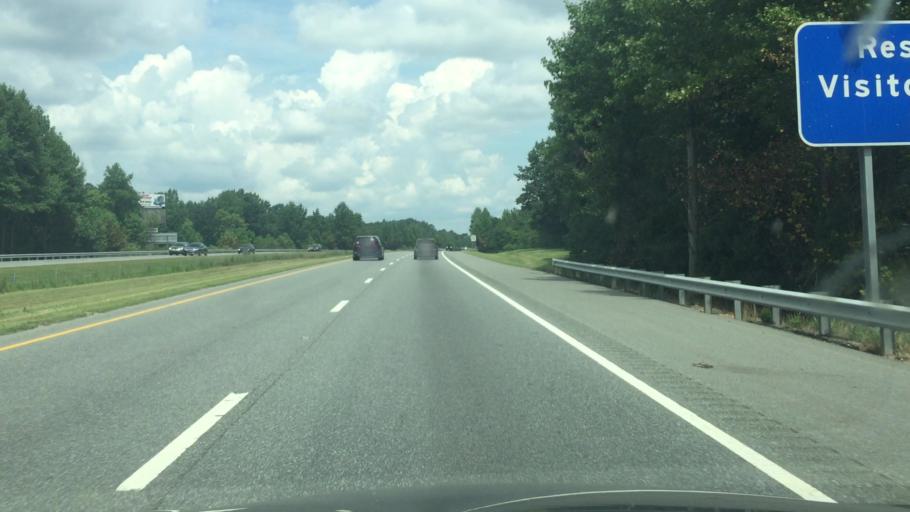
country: US
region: North Carolina
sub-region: Montgomery County
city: Biscoe
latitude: 35.4991
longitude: -79.7808
